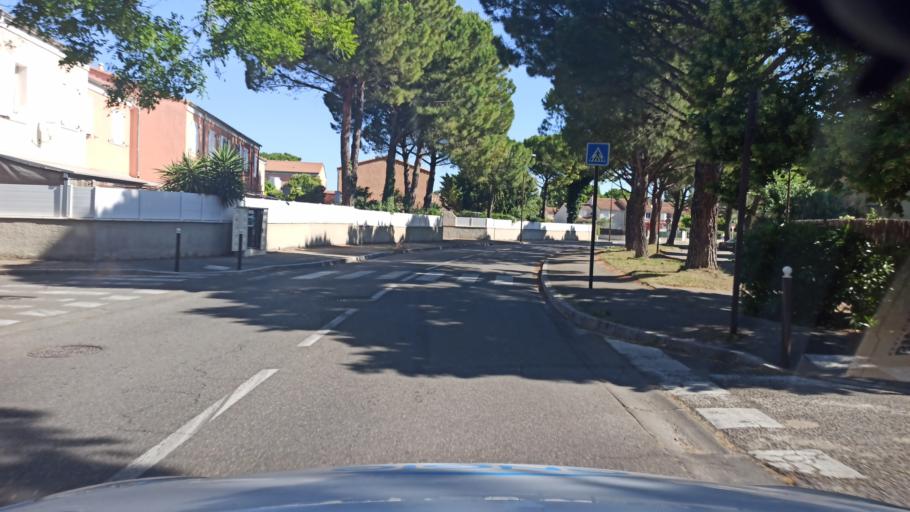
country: FR
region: Provence-Alpes-Cote d'Azur
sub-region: Departement du Vaucluse
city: Le Pontet
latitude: 43.9476
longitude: 4.8428
